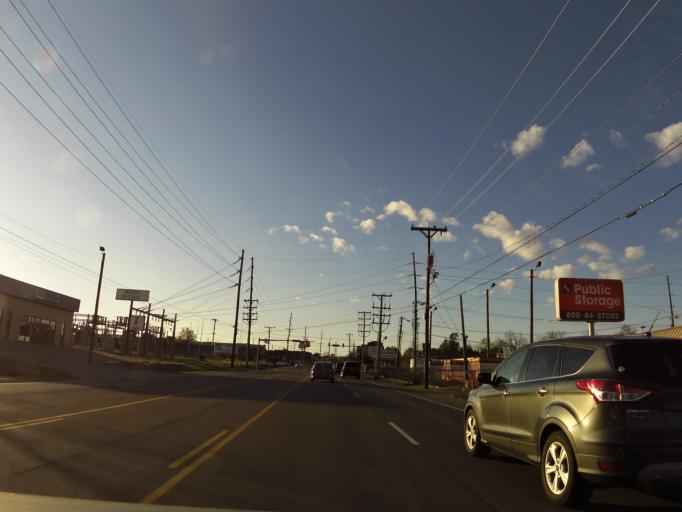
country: US
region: Tennessee
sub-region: Davidson County
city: Goodlettsville
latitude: 36.2932
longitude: -86.6957
